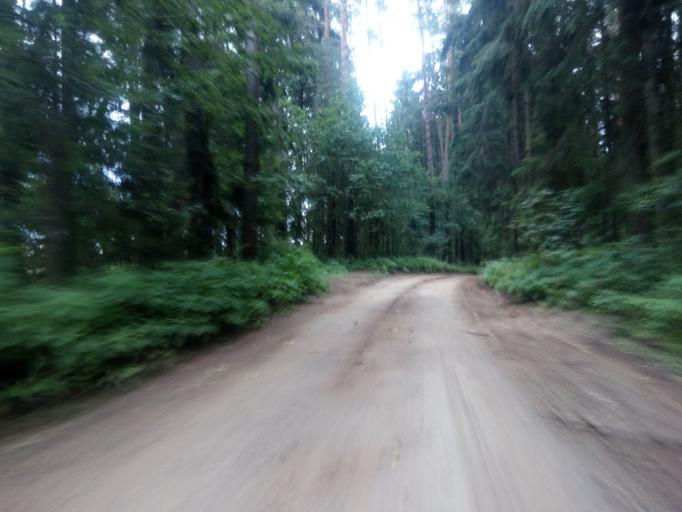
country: BY
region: Vitebsk
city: Dzisna
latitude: 55.7047
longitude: 28.3411
